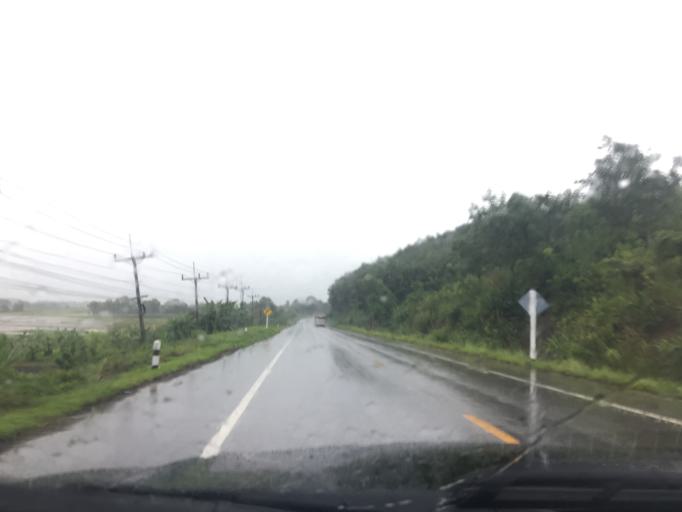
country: TH
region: Chiang Rai
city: Chiang Saen
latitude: 20.2664
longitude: 100.1914
